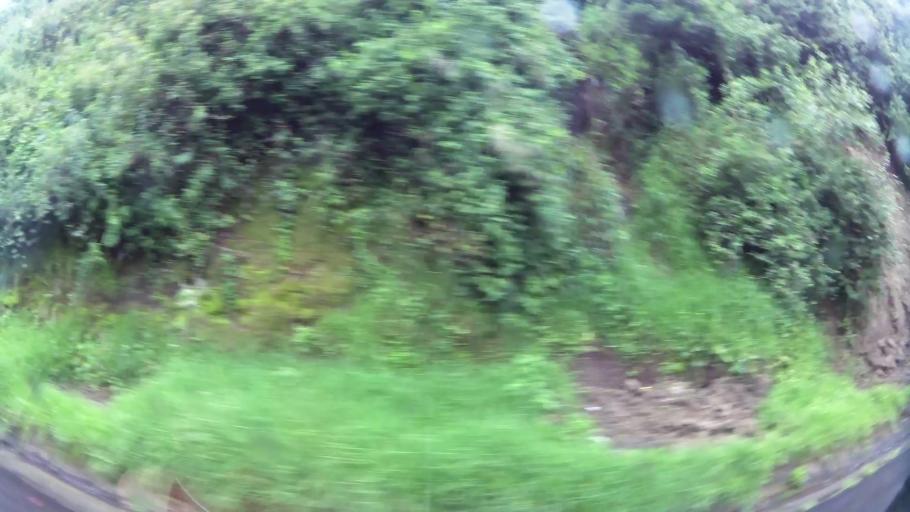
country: EC
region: Pichincha
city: Sangolqui
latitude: -0.2710
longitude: -78.4474
